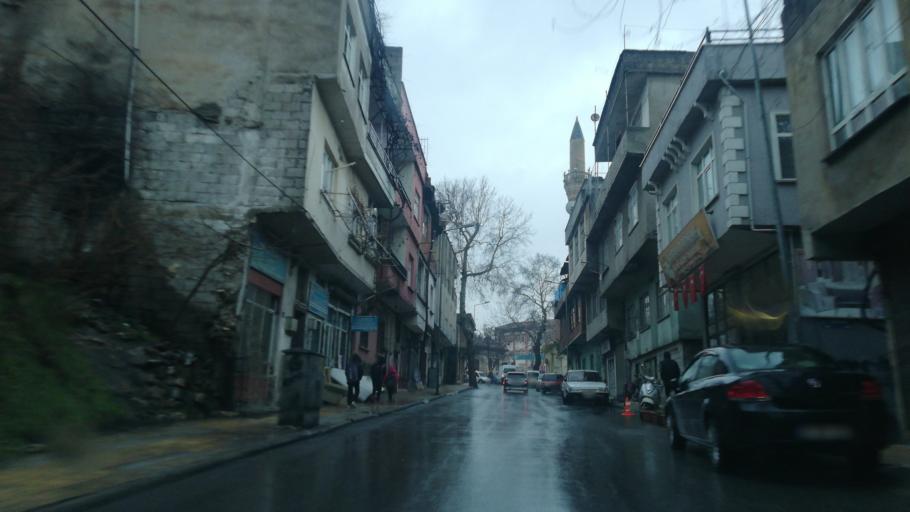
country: TR
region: Kahramanmaras
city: Kahramanmaras
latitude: 37.5858
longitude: 36.9292
